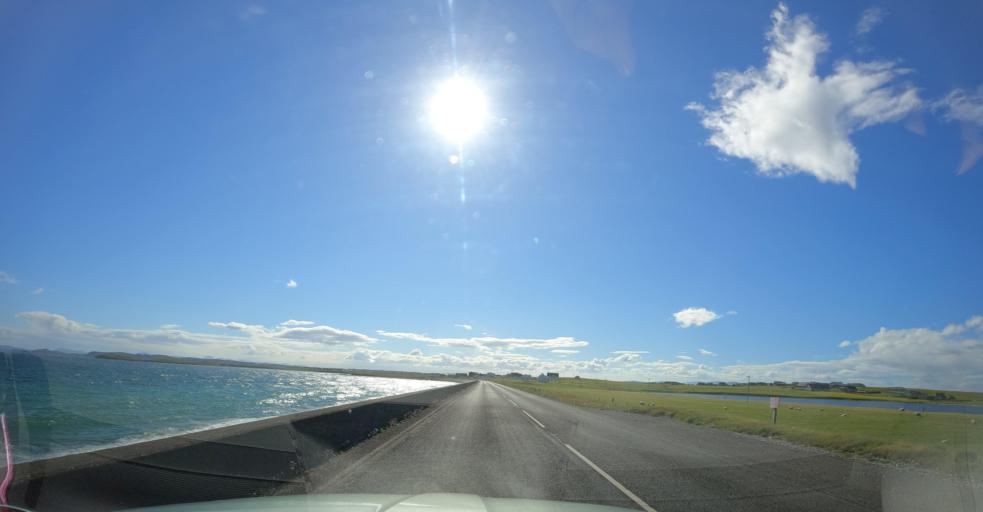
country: GB
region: Scotland
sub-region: Eilean Siar
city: Stornoway
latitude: 58.2061
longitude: -6.3005
